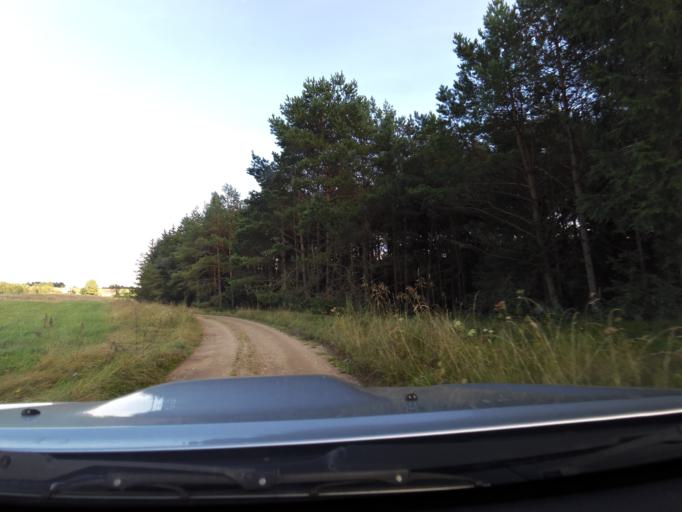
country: LT
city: Trakai
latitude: 54.6423
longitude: 24.9895
